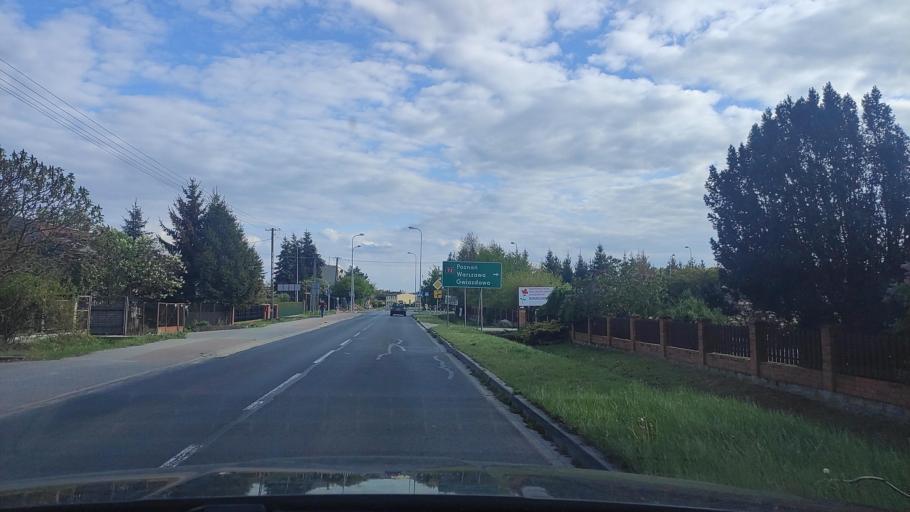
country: PL
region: Greater Poland Voivodeship
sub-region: Powiat poznanski
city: Kostrzyn
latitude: 52.4042
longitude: 17.2258
